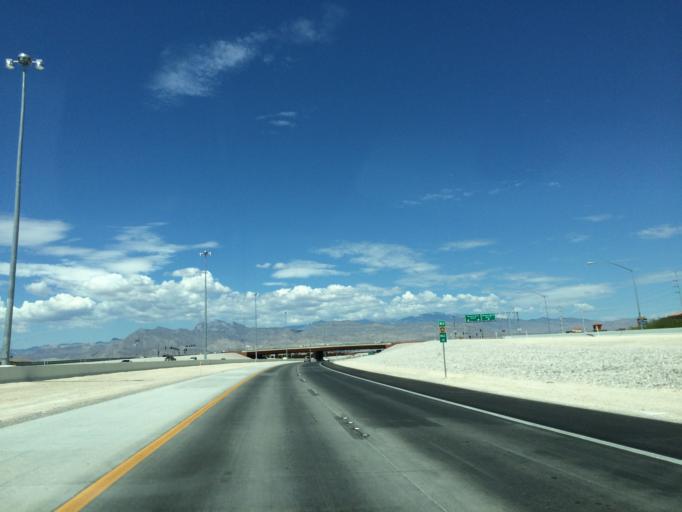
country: US
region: Nevada
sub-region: Clark County
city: North Las Vegas
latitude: 36.2755
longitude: -115.2019
